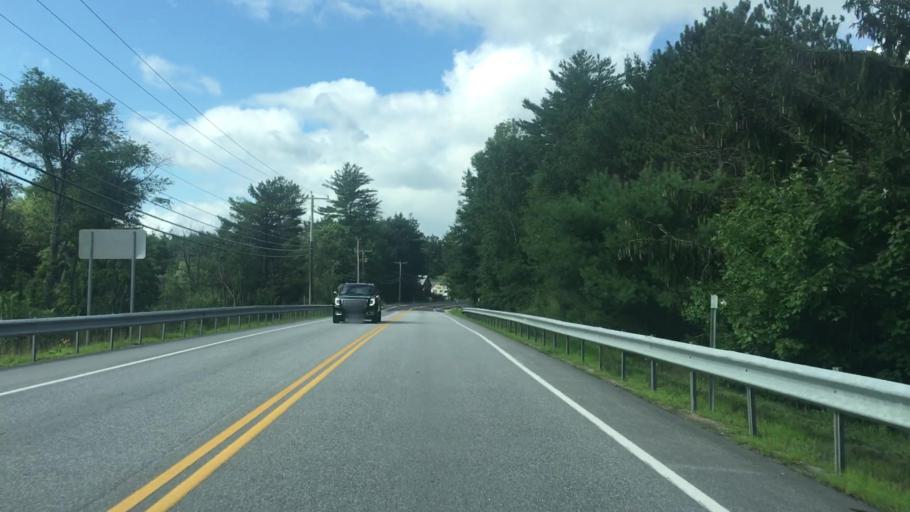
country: US
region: New Hampshire
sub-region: Belknap County
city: Gilford
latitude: 43.5478
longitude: -71.4079
